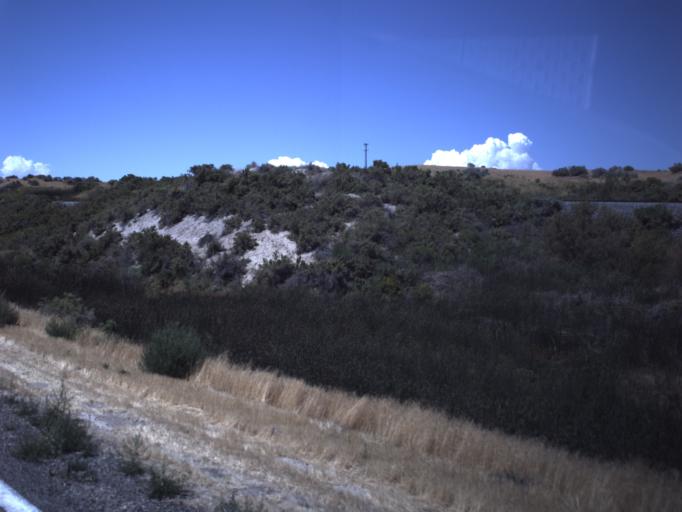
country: US
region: Utah
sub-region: Millard County
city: Delta
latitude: 39.5263
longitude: -112.3605
